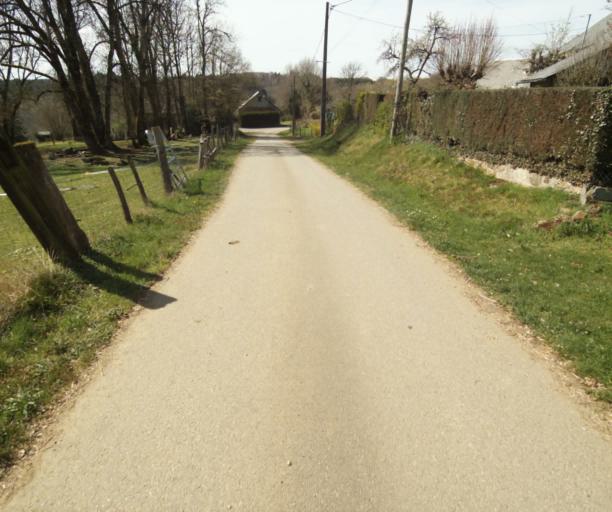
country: FR
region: Limousin
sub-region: Departement de la Correze
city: Seilhac
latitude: 45.4012
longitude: 1.7859
